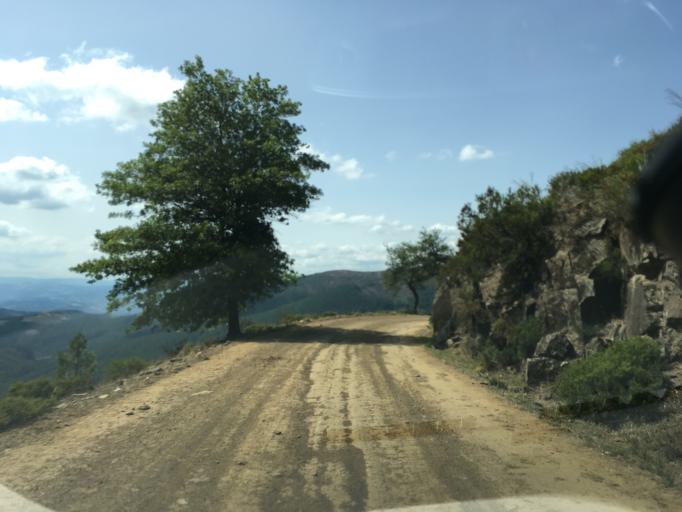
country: PT
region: Braga
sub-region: Celorico de Basto
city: Celorico de Basto
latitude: 41.2886
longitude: -7.9373
